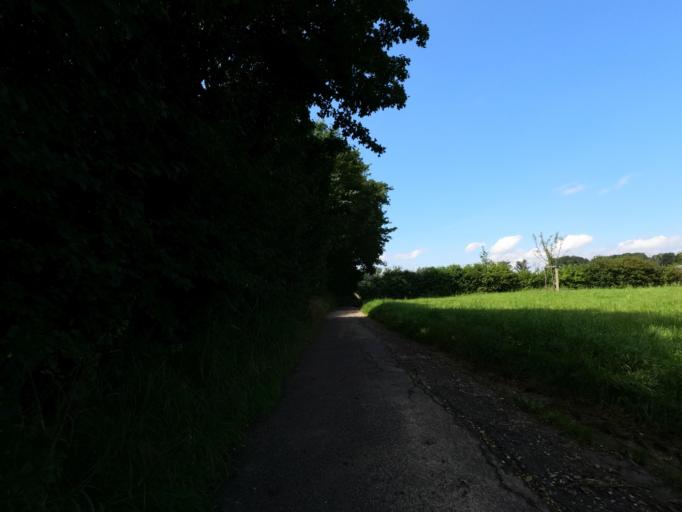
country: DE
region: North Rhine-Westphalia
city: Geilenkirchen
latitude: 50.9666
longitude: 6.1368
